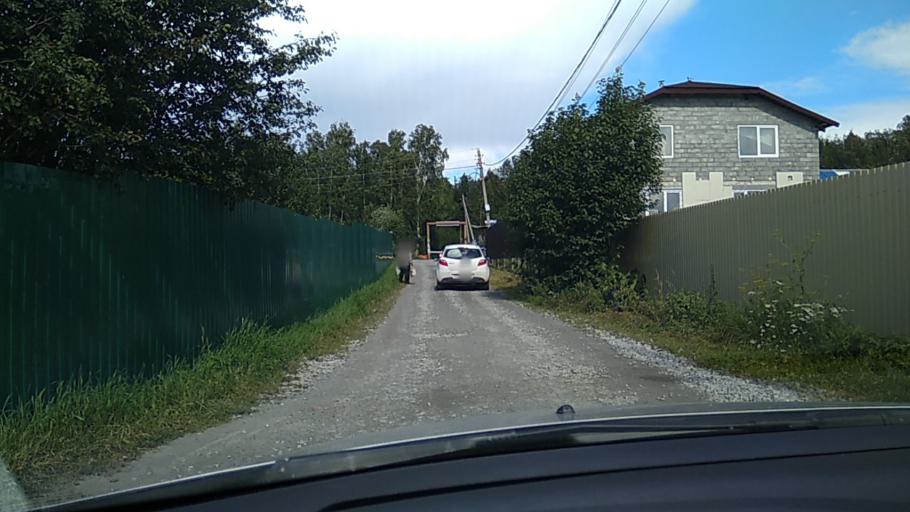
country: RU
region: Sverdlovsk
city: Sredneuralsk
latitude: 56.9692
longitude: 60.4693
